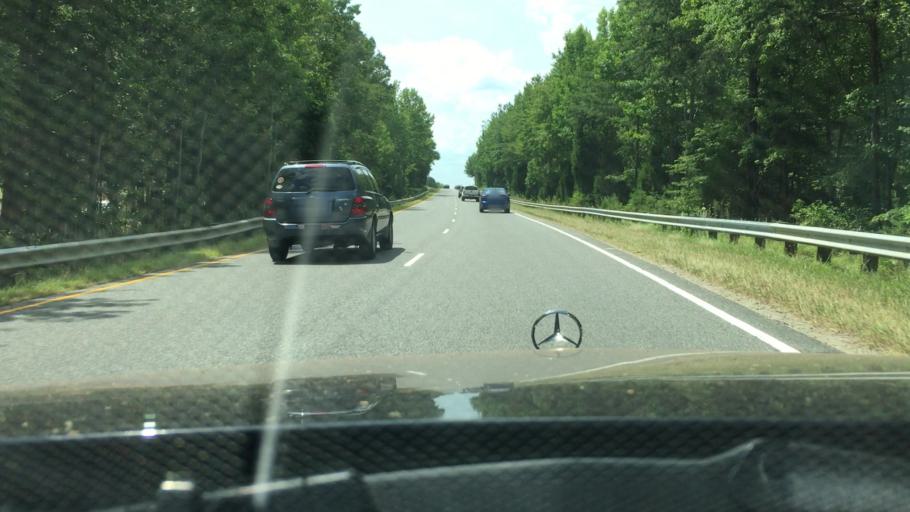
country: US
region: Virginia
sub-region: Spotsylvania County
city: Spotsylvania
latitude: 38.3193
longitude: -77.6919
